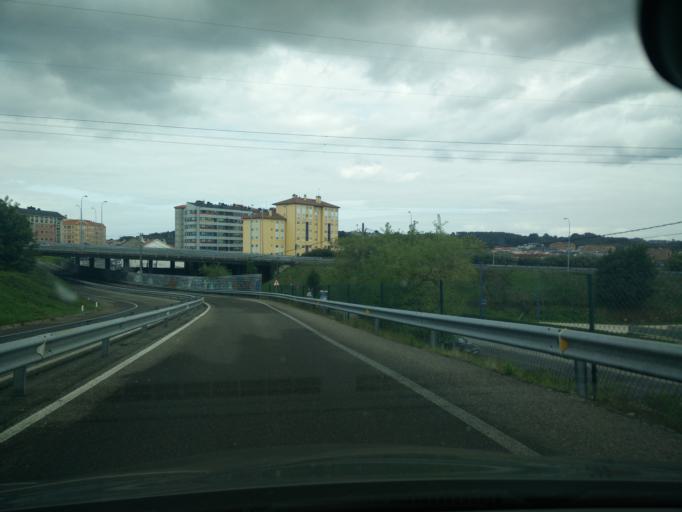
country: ES
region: Galicia
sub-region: Provincia da Coruna
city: Cambre
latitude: 43.3117
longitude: -8.3646
